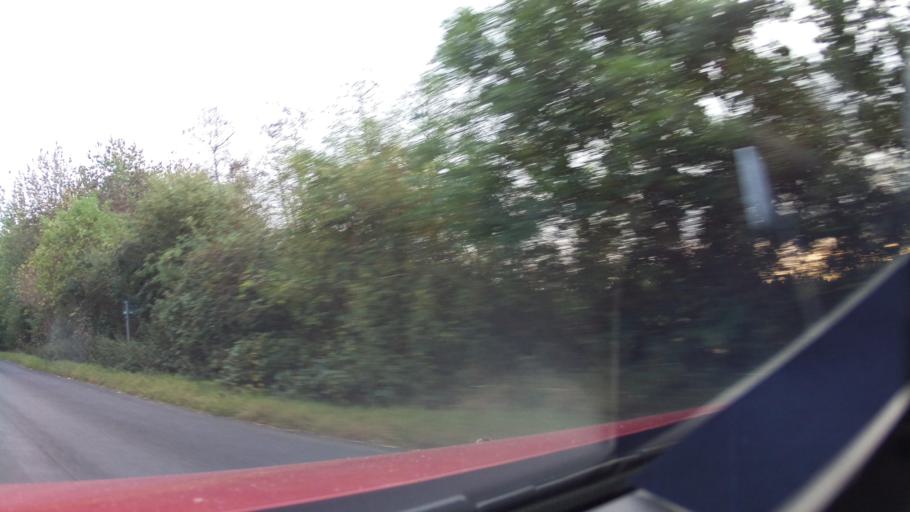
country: GB
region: England
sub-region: Nottinghamshire
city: South Collingham
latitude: 53.1454
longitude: -0.6687
